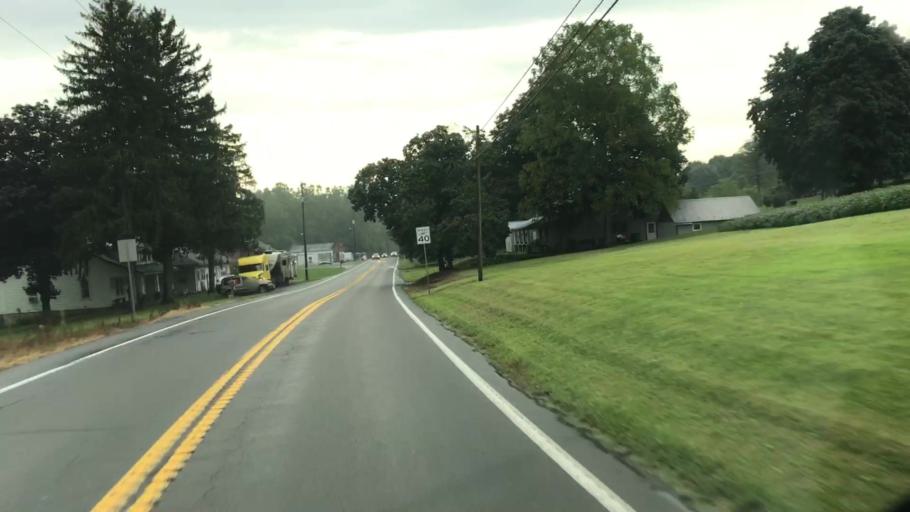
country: US
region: Pennsylvania
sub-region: Cumberland County
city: Schlusser
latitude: 40.3253
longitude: -77.1760
